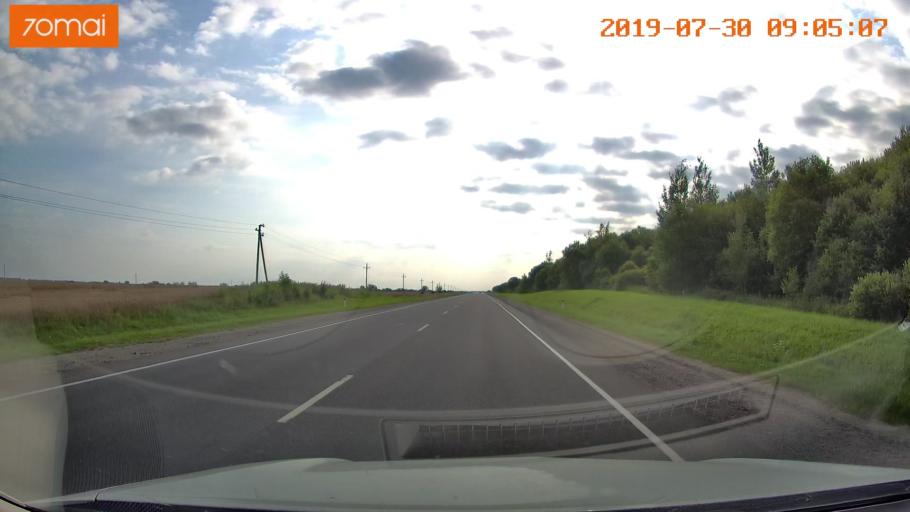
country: RU
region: Kaliningrad
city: Gusev
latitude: 54.6065
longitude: 22.2994
